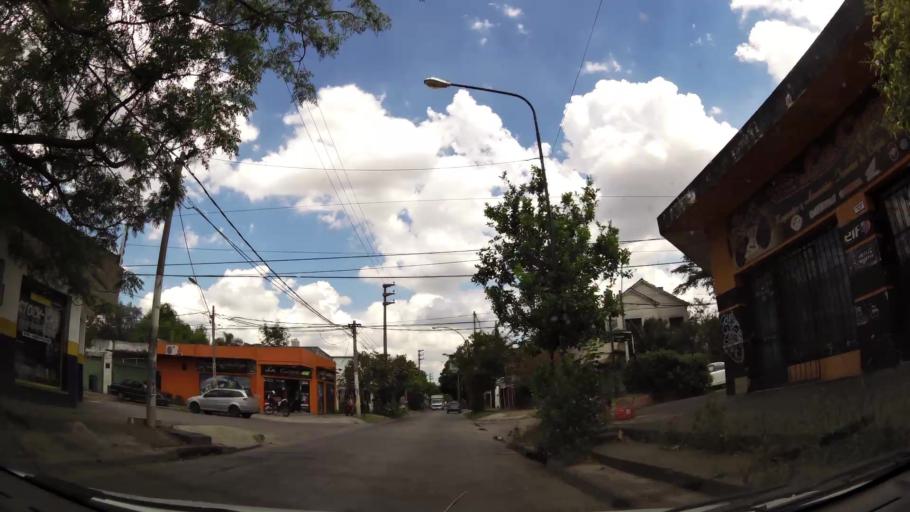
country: AR
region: Buenos Aires
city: Ituzaingo
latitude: -34.6505
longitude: -58.6766
